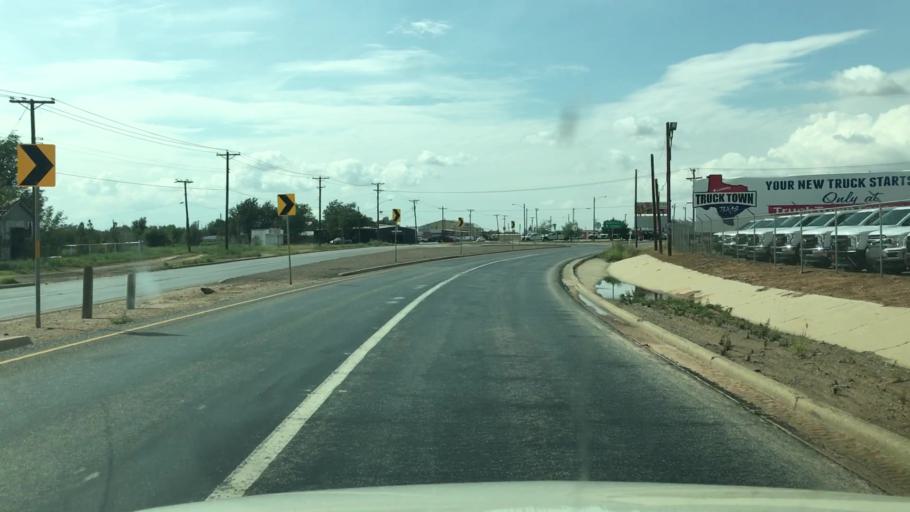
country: US
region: Texas
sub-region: Dawson County
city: Lamesa
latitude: 32.7194
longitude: -101.9444
